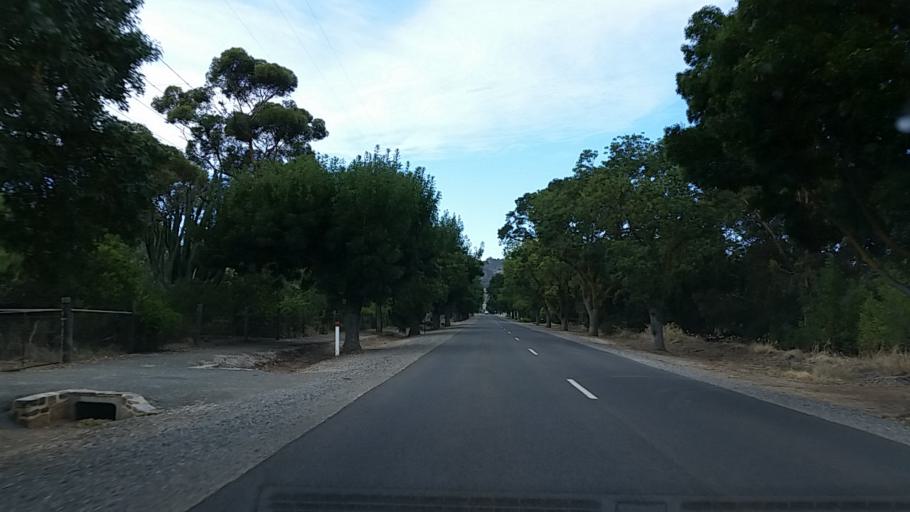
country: AU
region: South Australia
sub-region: Barossa
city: Tanunda
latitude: -34.5387
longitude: 138.9721
